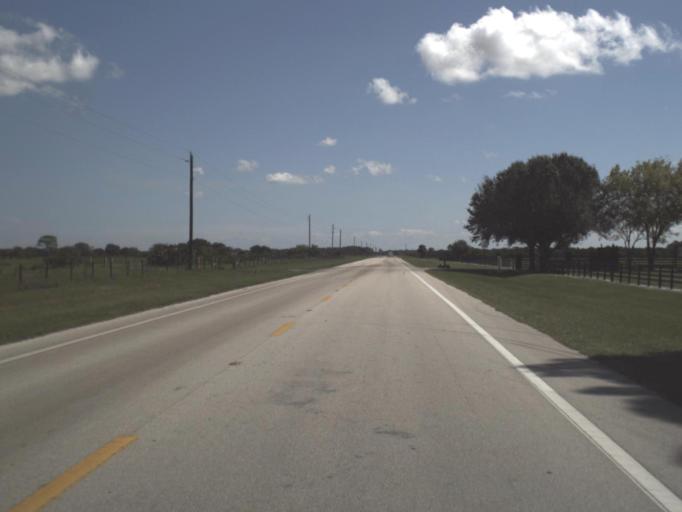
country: US
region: Florida
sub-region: Hendry County
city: Port LaBelle
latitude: 26.8120
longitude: -81.3989
